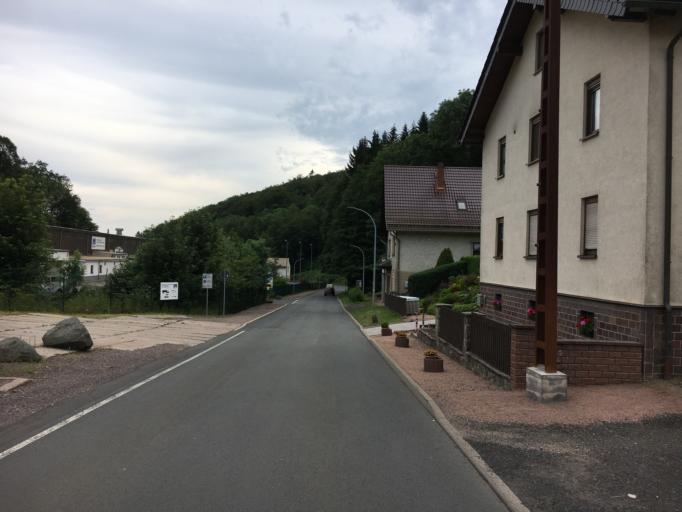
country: DE
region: Thuringia
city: Brotterode
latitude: 50.8177
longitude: 10.4295
